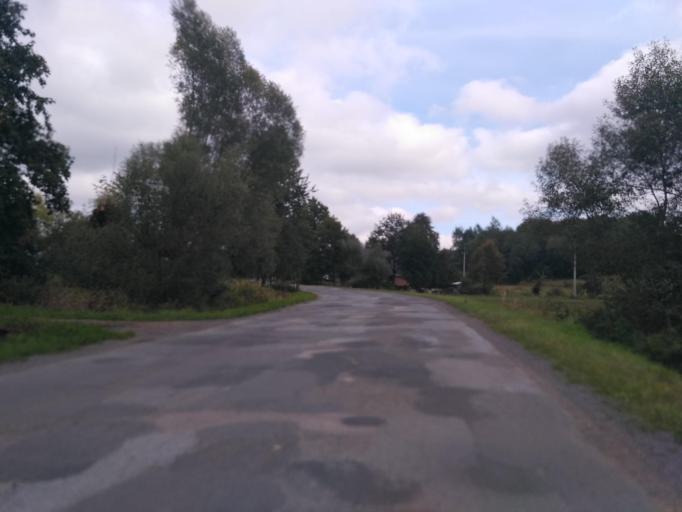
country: PL
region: Subcarpathian Voivodeship
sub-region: Powiat ropczycko-sedziszowski
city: Niedzwiada
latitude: 49.9297
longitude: 21.4726
